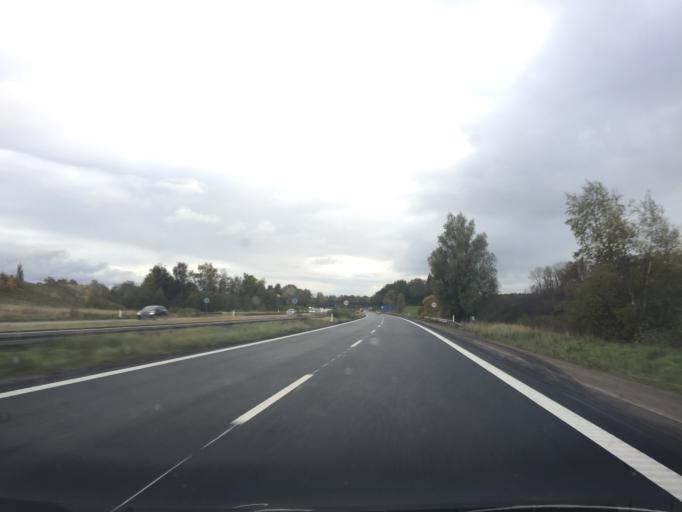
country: DK
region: Capital Region
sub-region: Fredensborg Kommune
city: Kokkedal
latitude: 55.9155
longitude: 12.4716
